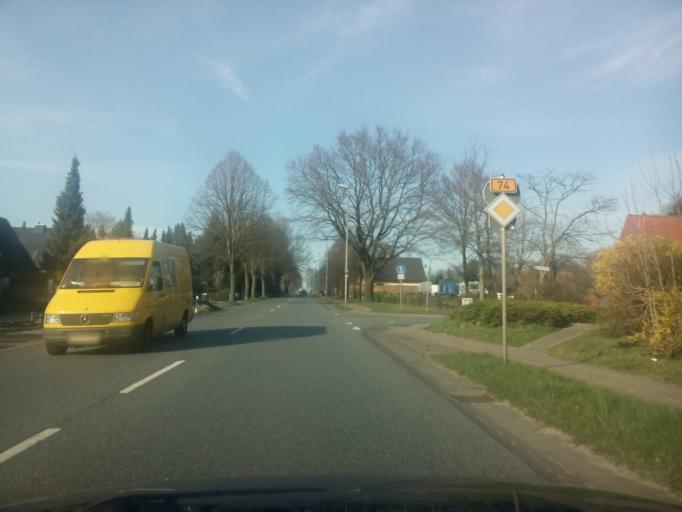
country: DE
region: Lower Saxony
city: Ritterhude
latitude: 53.1883
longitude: 8.7464
